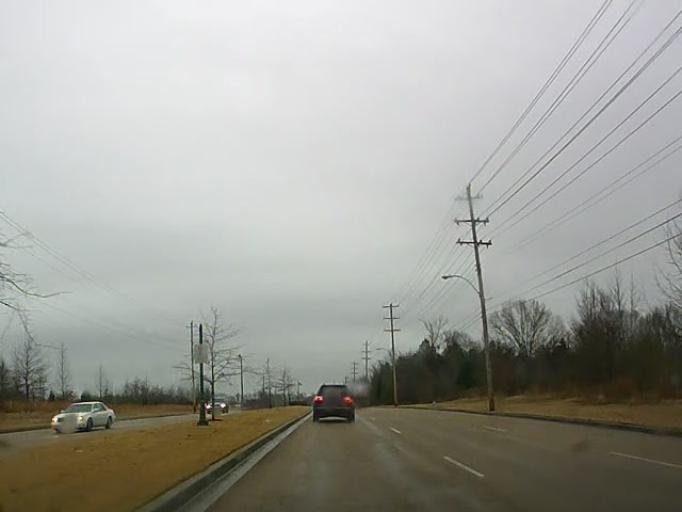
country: US
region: Tennessee
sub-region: Shelby County
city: Collierville
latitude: 35.0471
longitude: -89.7385
